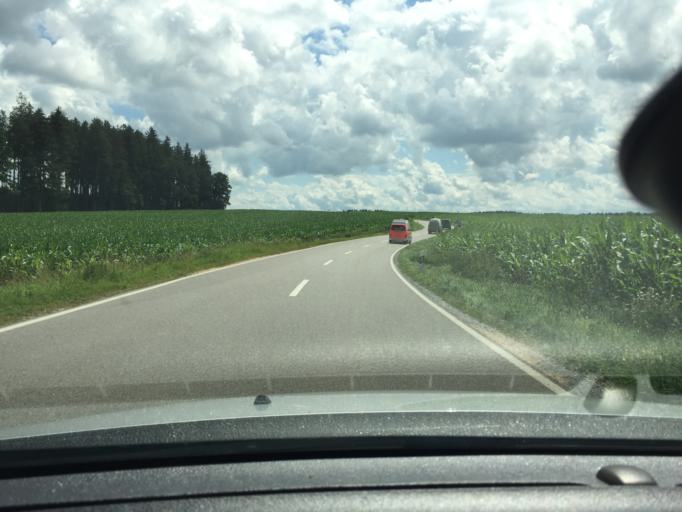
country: DE
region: Bavaria
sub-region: Upper Bavaria
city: Kienberg
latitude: 48.0547
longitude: 12.4996
